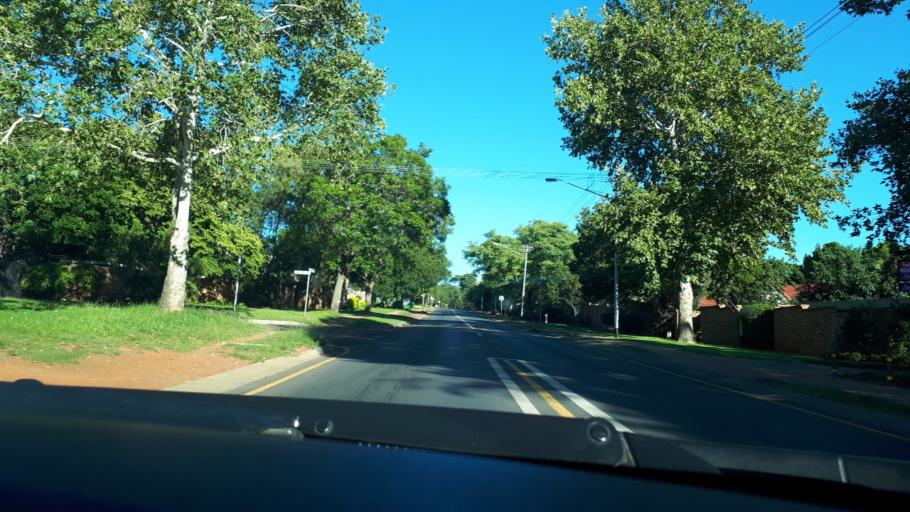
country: ZA
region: Gauteng
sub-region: City of Tshwane Metropolitan Municipality
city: Pretoria
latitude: -25.7733
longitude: 28.2816
